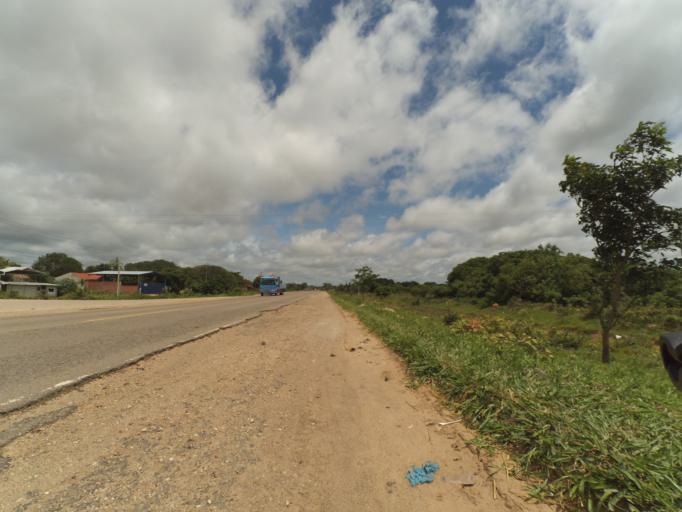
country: BO
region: Santa Cruz
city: Santa Rita
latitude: -17.8807
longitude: -63.2668
